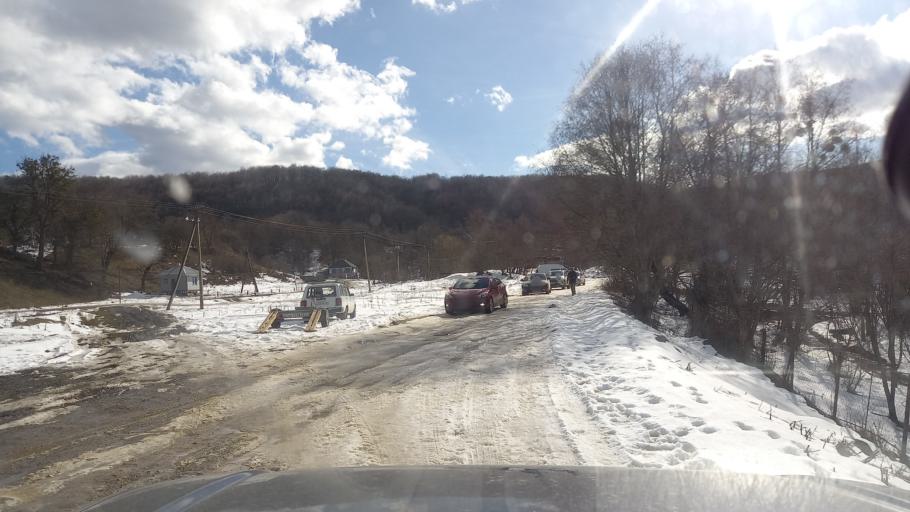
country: RU
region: Adygeya
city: Kamennomostskiy
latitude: 44.1965
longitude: 39.9603
